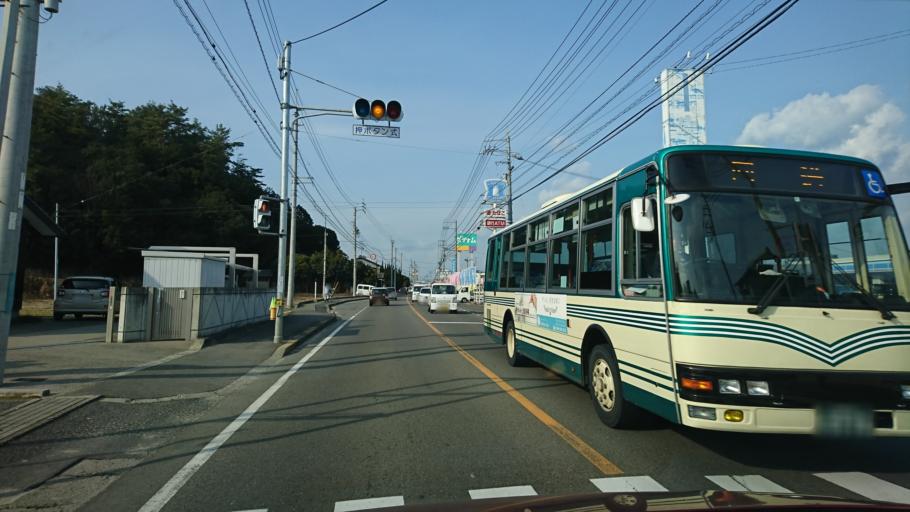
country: JP
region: Ehime
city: Saijo
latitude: 34.0293
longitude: 133.0368
